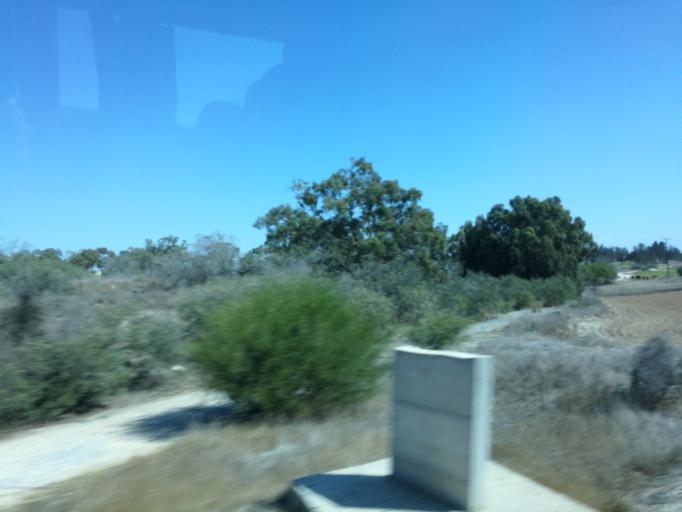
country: CY
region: Ammochostos
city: Acheritou
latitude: 35.0793
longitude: 33.8689
